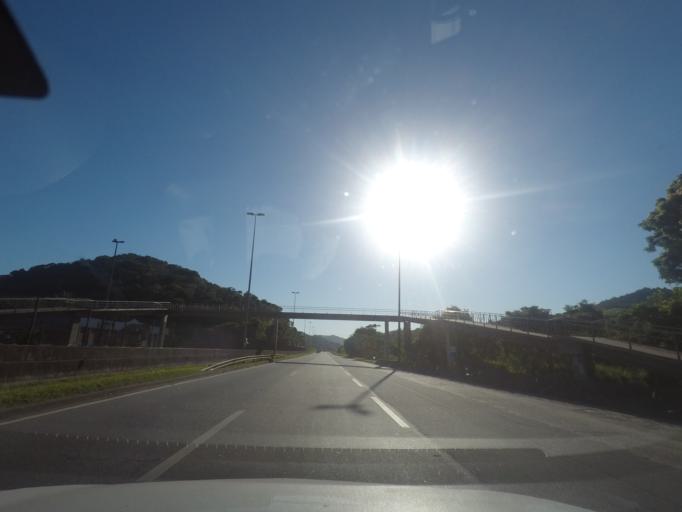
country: BR
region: Rio de Janeiro
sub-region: Petropolis
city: Petropolis
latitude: -22.6537
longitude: -43.1523
